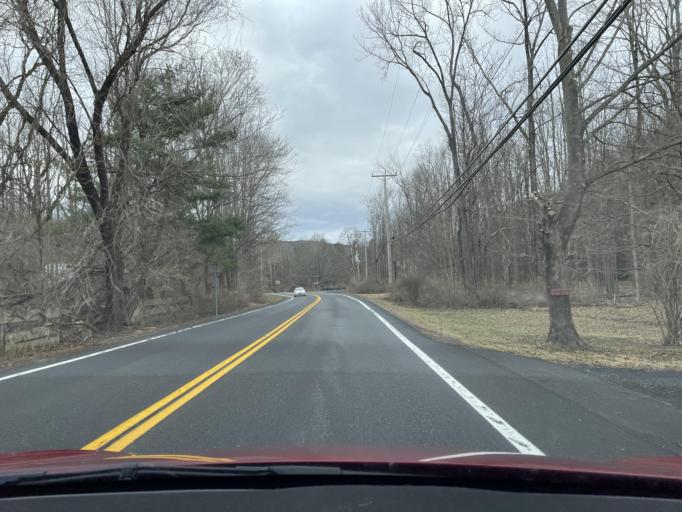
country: US
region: New York
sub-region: Ulster County
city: Woodstock
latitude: 42.0572
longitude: -74.1583
